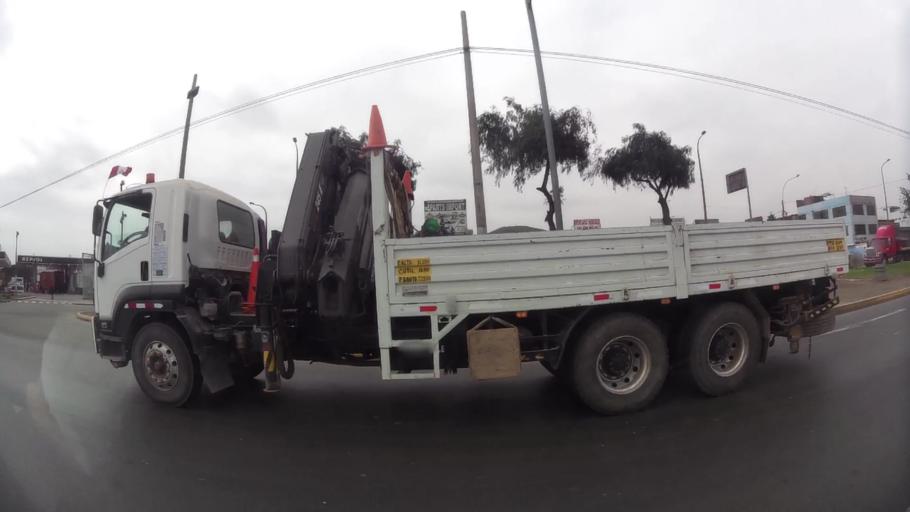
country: PE
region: Callao
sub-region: Callao
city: Callao
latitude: -11.9979
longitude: -77.1239
